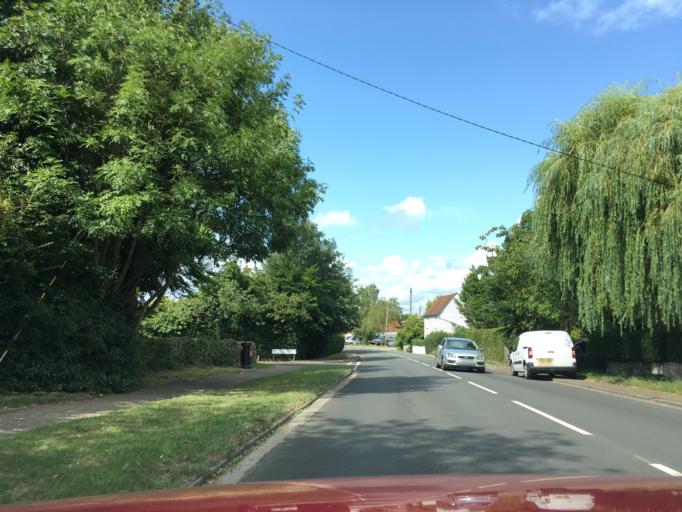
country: GB
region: England
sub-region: Kent
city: Headcorn
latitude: 51.1162
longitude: 0.6440
